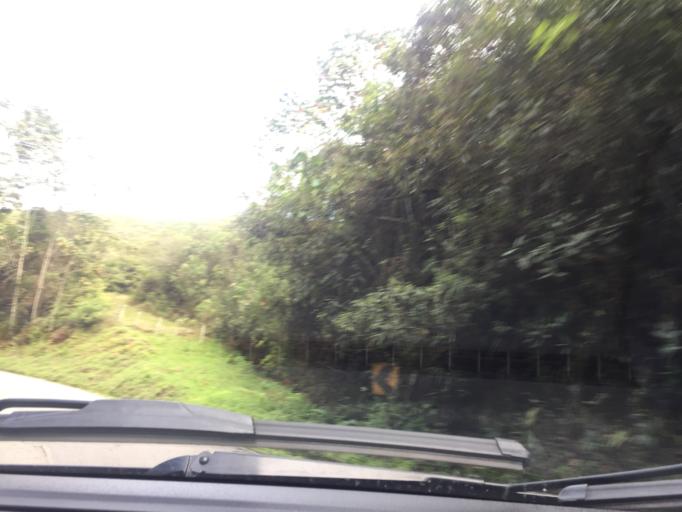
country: CO
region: Cundinamarca
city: Supata
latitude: 5.0266
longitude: -74.2725
